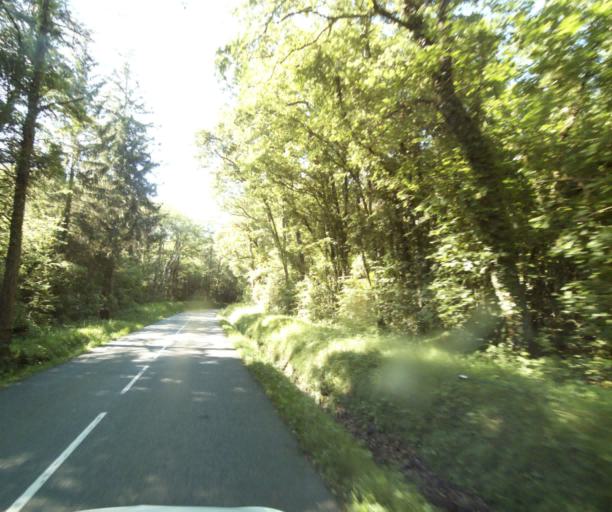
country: FR
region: Rhone-Alpes
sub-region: Departement de la Haute-Savoie
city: Ballaison
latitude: 46.2852
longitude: 6.3435
